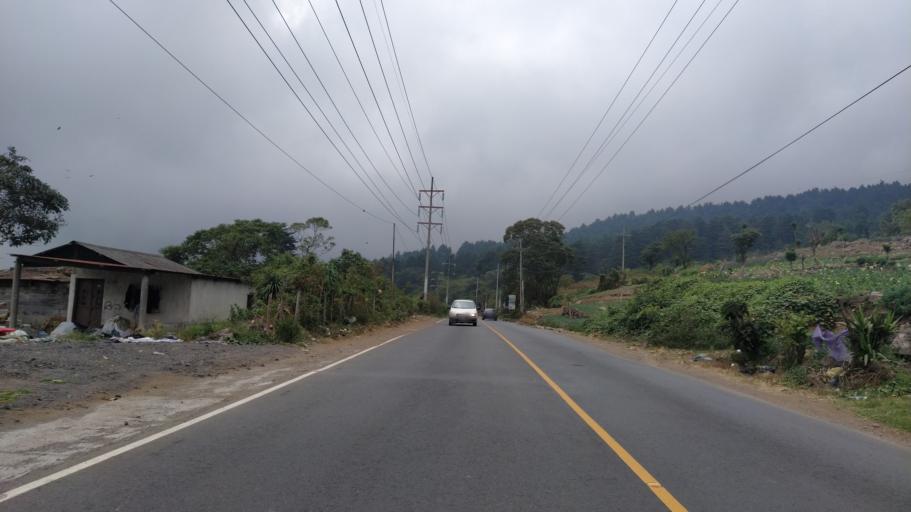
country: GT
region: Quetzaltenango
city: Zunil
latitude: 14.7458
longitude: -91.5131
